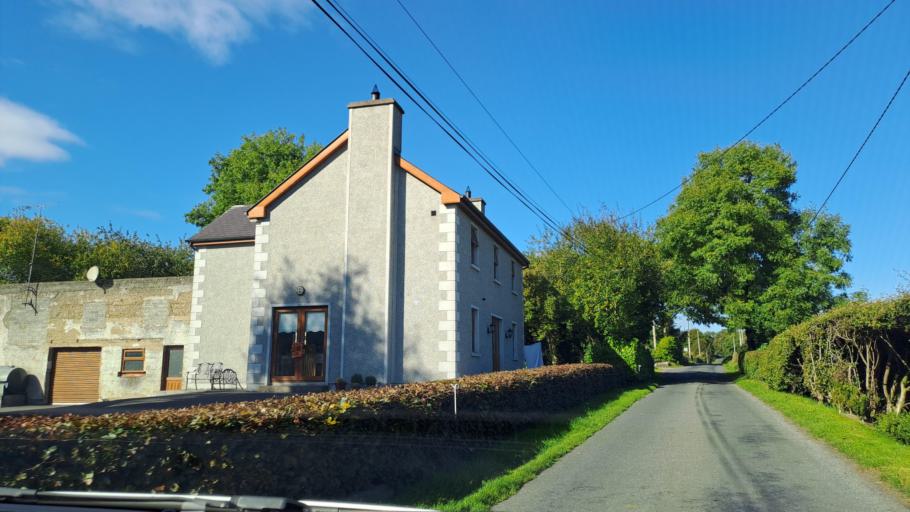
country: IE
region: Ulster
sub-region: County Monaghan
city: Carrickmacross
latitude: 53.9876
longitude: -6.7483
